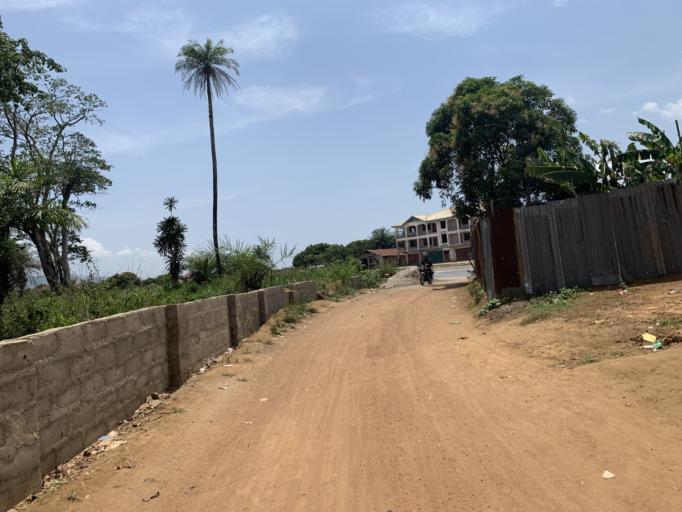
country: SL
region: Western Area
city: Waterloo
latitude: 8.3348
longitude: -13.0245
